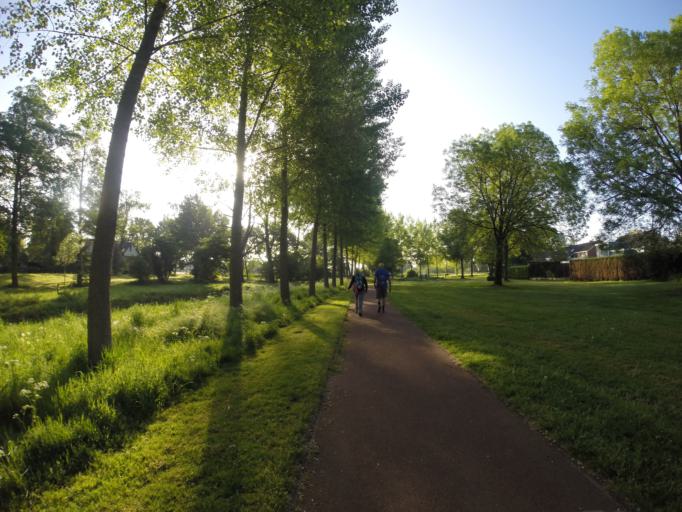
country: NL
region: Gelderland
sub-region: Oude IJsselstreek
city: Gendringen
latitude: 51.9248
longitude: 6.3475
